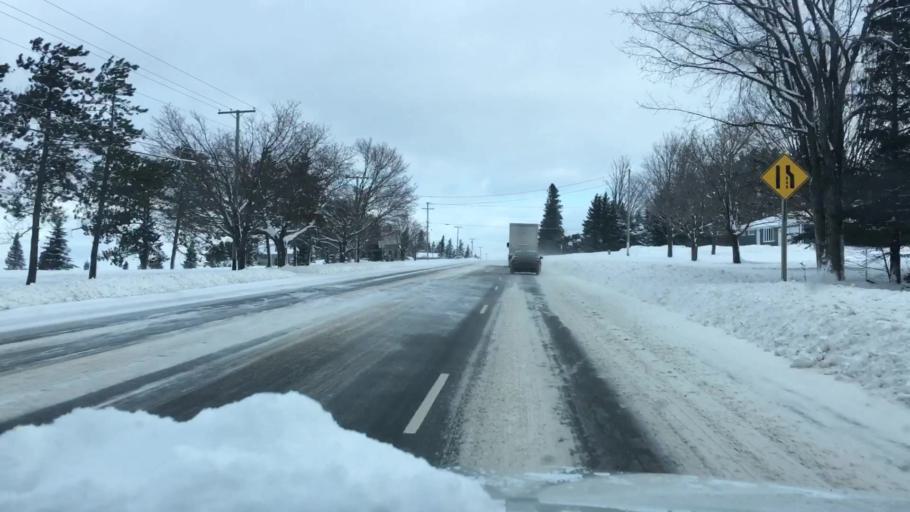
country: US
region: Maine
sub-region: Aroostook County
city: Presque Isle
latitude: 46.7265
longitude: -68.0038
